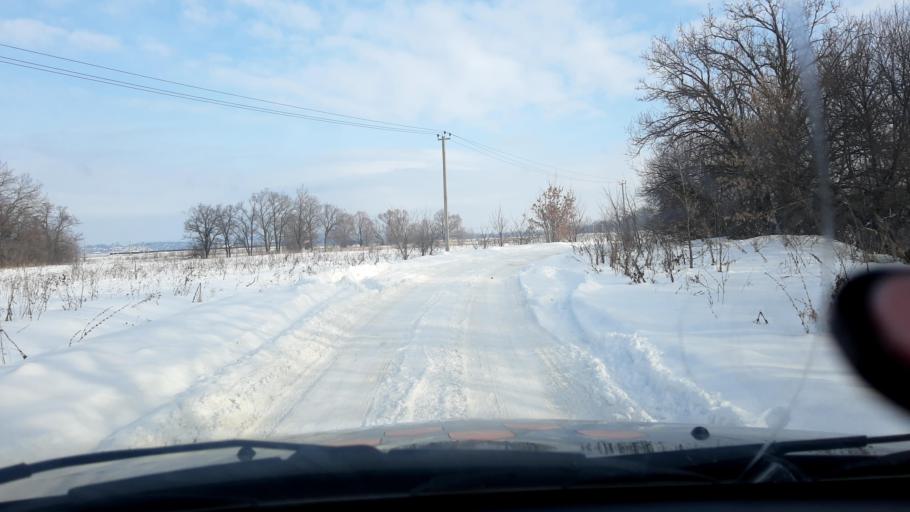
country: RU
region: Bashkortostan
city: Avdon
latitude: 54.4956
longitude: 55.8592
